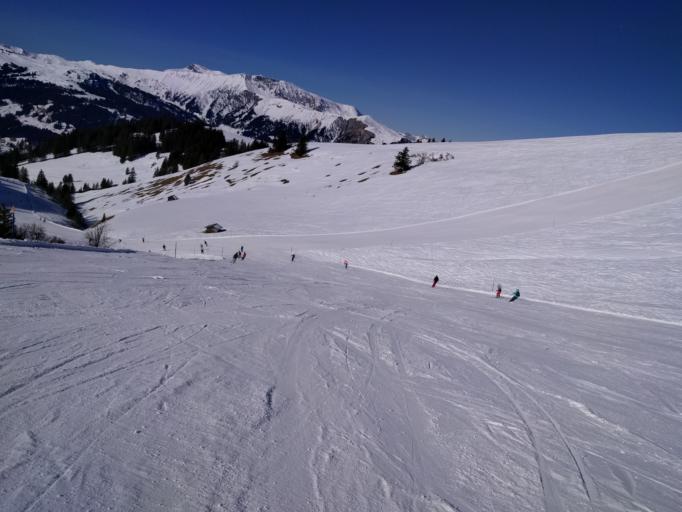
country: CH
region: Bern
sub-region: Obersimmental-Saanen District
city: Lenk
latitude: 46.4507
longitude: 7.4910
